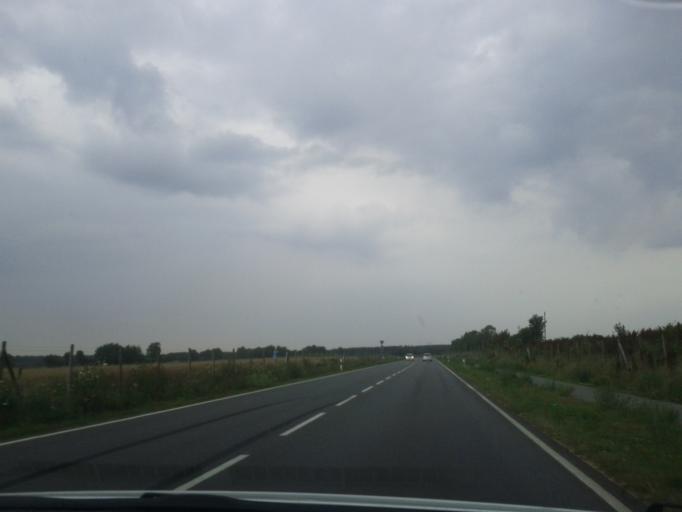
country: DE
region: Lower Saxony
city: Agathenburg
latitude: 53.5477
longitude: 9.4968
